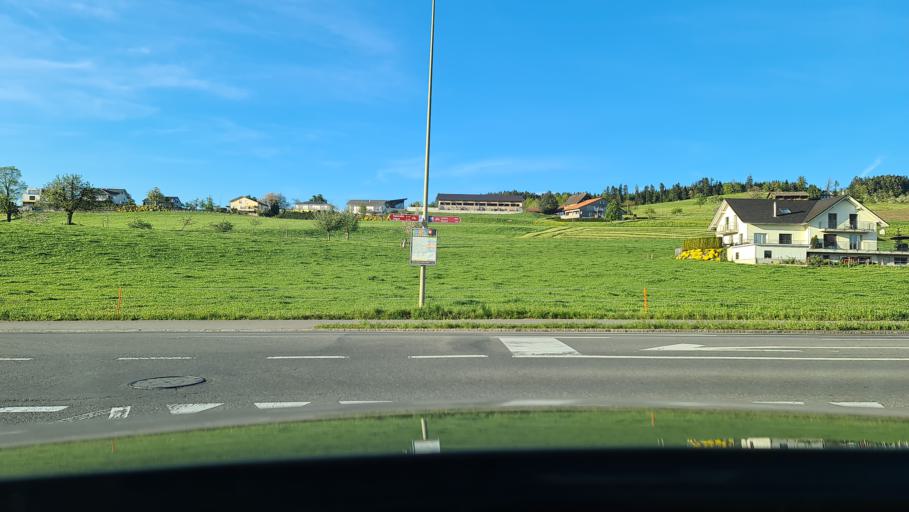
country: CH
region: Lucerne
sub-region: Sursee District
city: Ruswil
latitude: 47.0906
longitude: 8.1063
